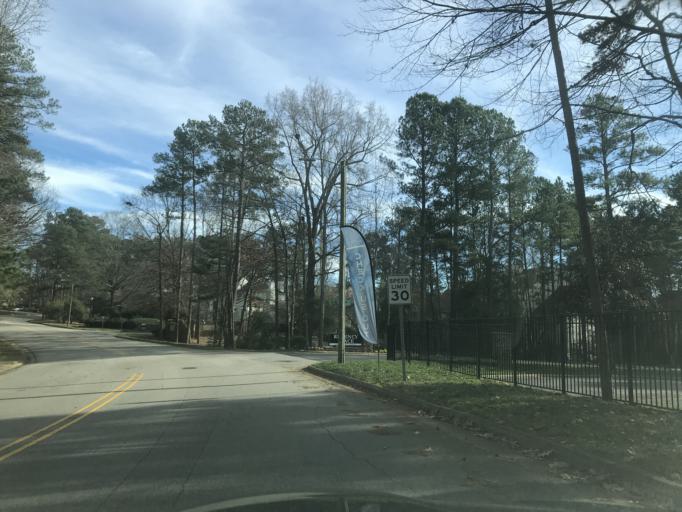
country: US
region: North Carolina
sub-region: Wake County
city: Cary
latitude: 35.7777
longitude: -78.7433
